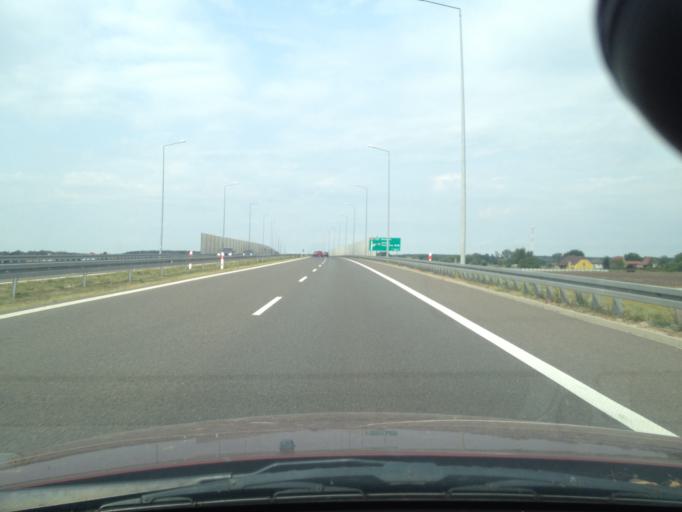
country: PL
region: West Pomeranian Voivodeship
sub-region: Powiat pyrzycki
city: Lipiany
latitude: 52.9477
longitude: 14.9621
